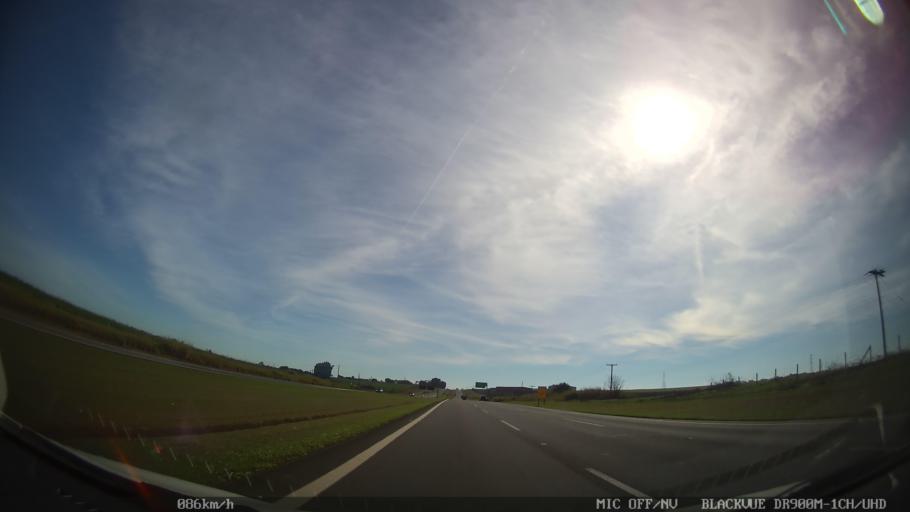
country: BR
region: Sao Paulo
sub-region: Cordeiropolis
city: Cordeiropolis
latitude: -22.4724
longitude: -47.3989
